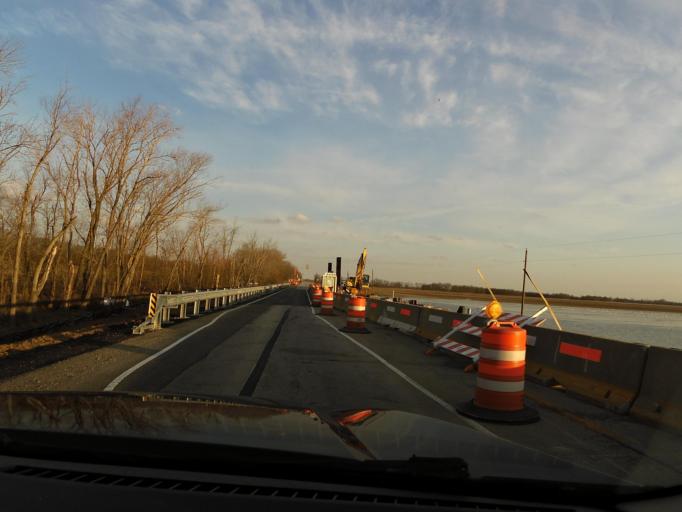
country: US
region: Illinois
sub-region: Fayette County
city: Vandalia
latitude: 38.9124
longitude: -89.0857
